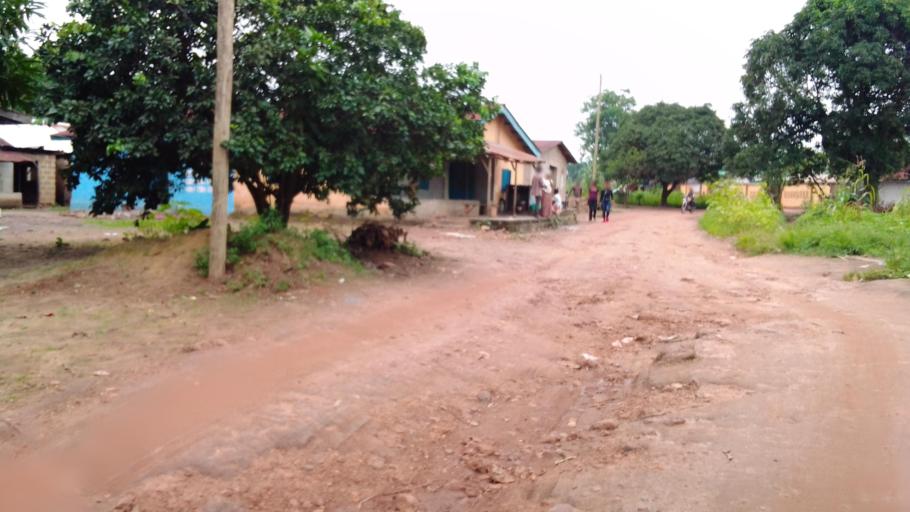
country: SL
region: Eastern Province
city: Kenema
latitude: 7.8597
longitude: -11.2057
